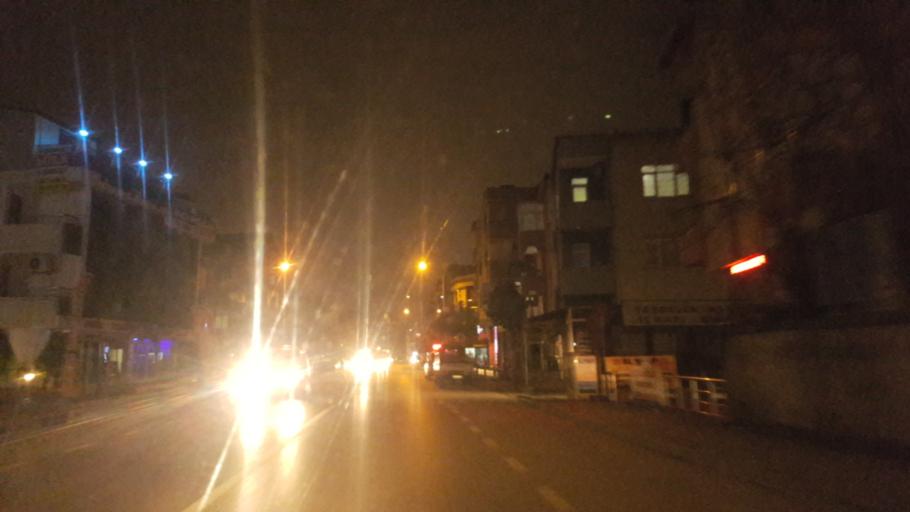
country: TR
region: Kocaeli
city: Darica
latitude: 40.7807
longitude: 29.3930
